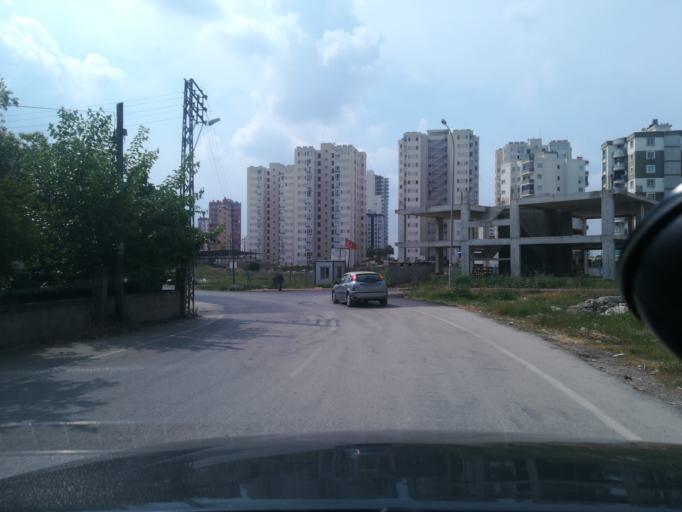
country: TR
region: Adana
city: Seyhan
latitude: 37.0263
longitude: 35.2802
